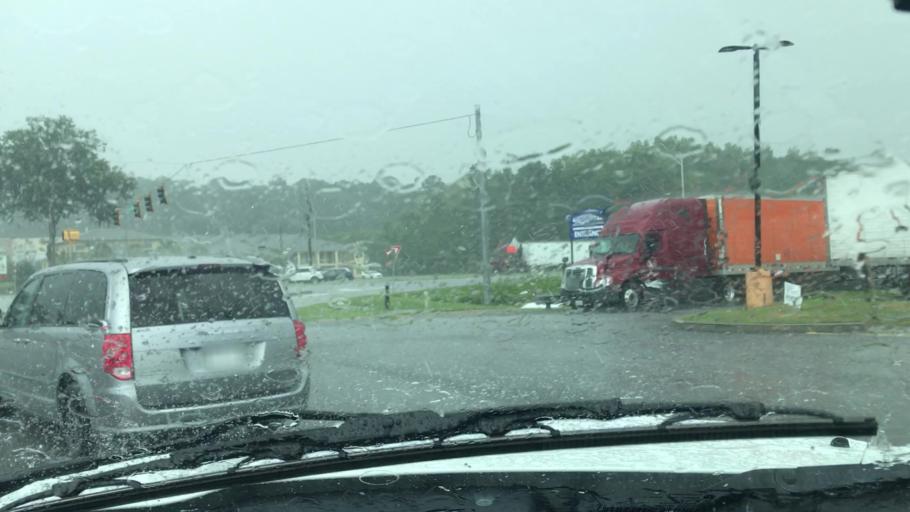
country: US
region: Georgia
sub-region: Chatham County
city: Port Wentworth
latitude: 32.1883
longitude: -81.1945
